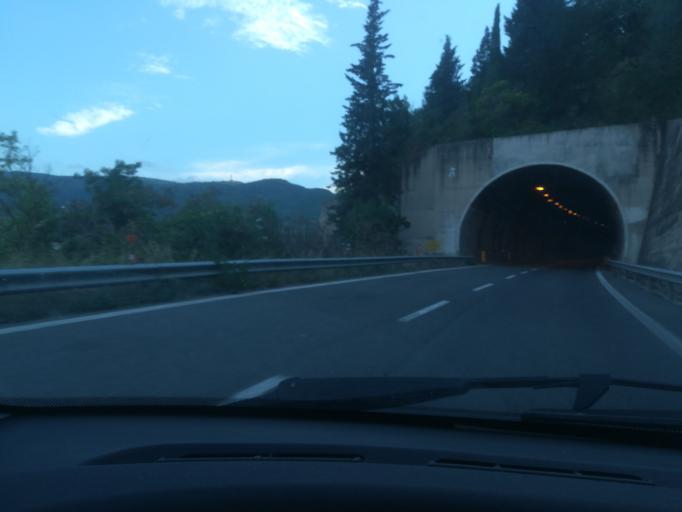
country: IT
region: The Marches
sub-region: Provincia di Macerata
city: Caldarola
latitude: 43.1488
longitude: 13.2108
